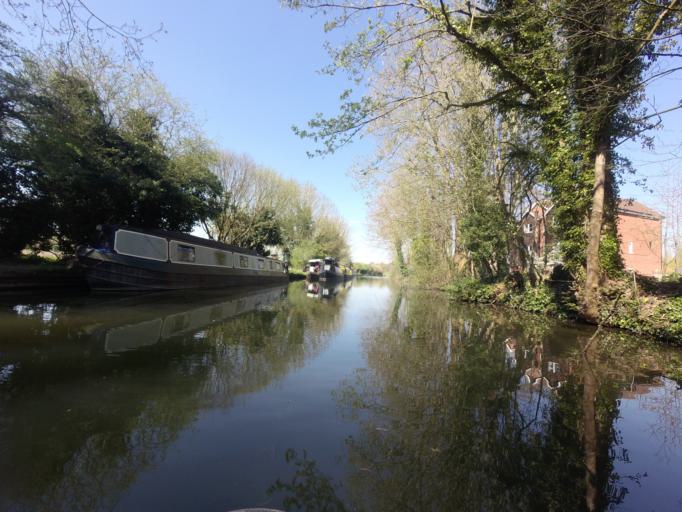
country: GB
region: England
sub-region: Hertfordshire
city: Abbots Langley
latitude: 51.6944
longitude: -0.4369
